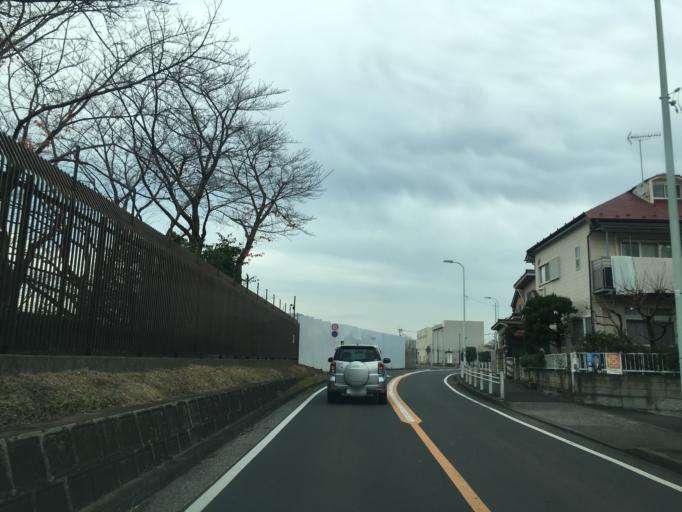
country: JP
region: Tokyo
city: Higashimurayama-shi
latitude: 35.7533
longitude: 139.4617
